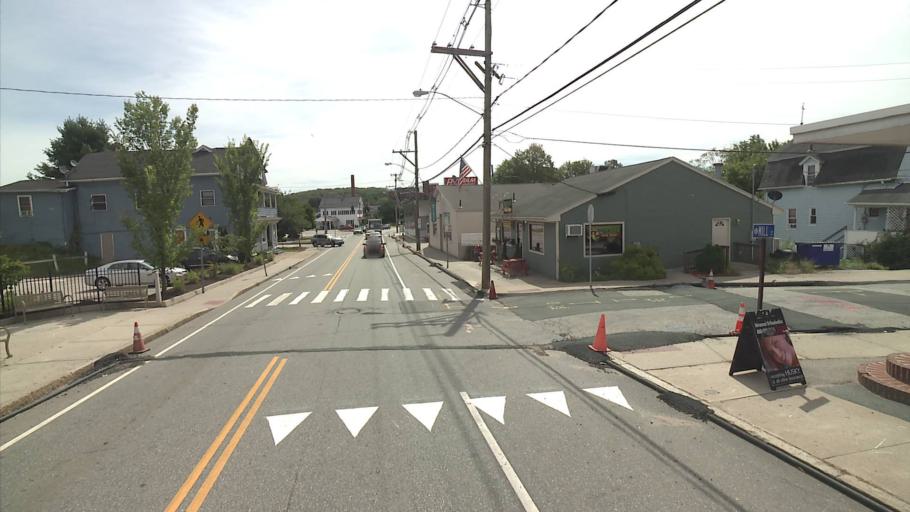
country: US
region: Connecticut
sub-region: Windham County
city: Putnam
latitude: 41.9238
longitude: -71.9096
